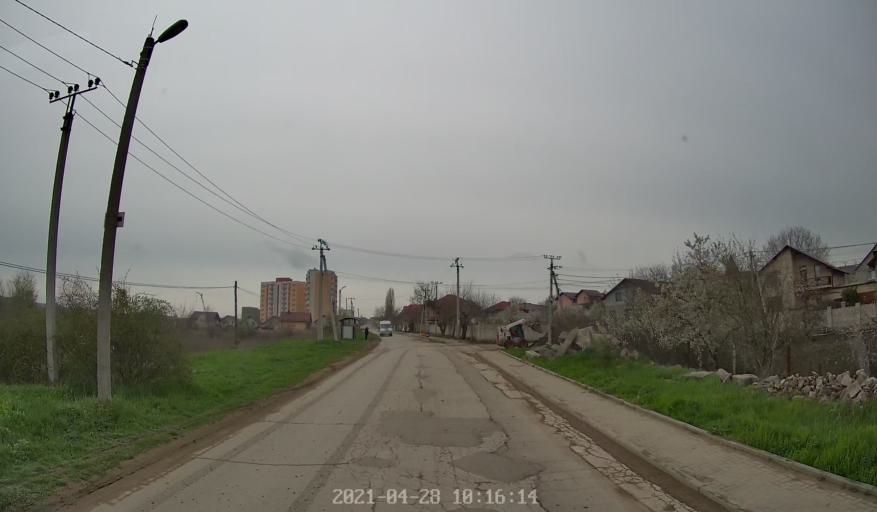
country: MD
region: Chisinau
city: Chisinau
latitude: 46.9901
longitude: 28.9339
